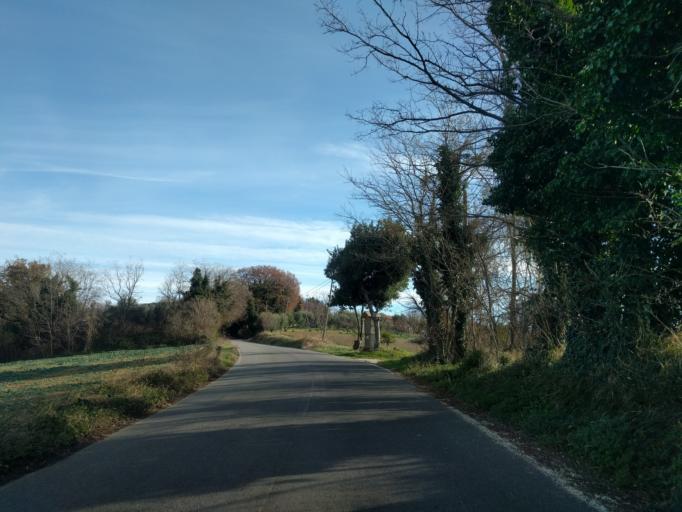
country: IT
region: The Marches
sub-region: Provincia di Pesaro e Urbino
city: Cuccurano
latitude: 43.8033
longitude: 12.9571
